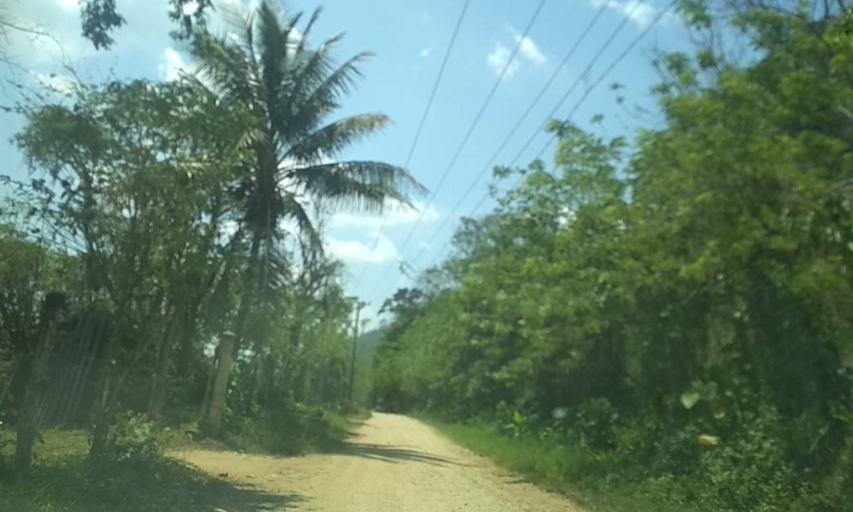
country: MX
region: Chiapas
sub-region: Tecpatan
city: Raudales Malpaso
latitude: 17.2881
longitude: -93.8408
